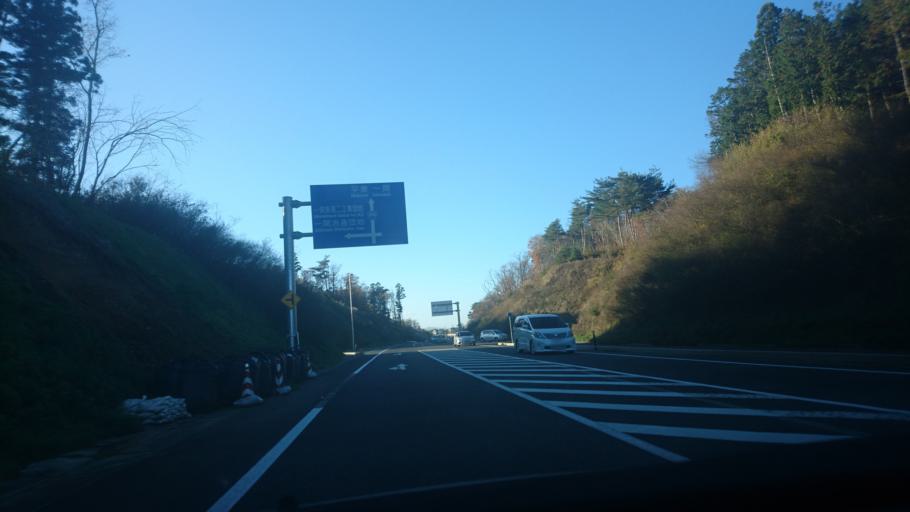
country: JP
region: Iwate
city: Ichinoseki
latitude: 38.9044
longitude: 141.1741
